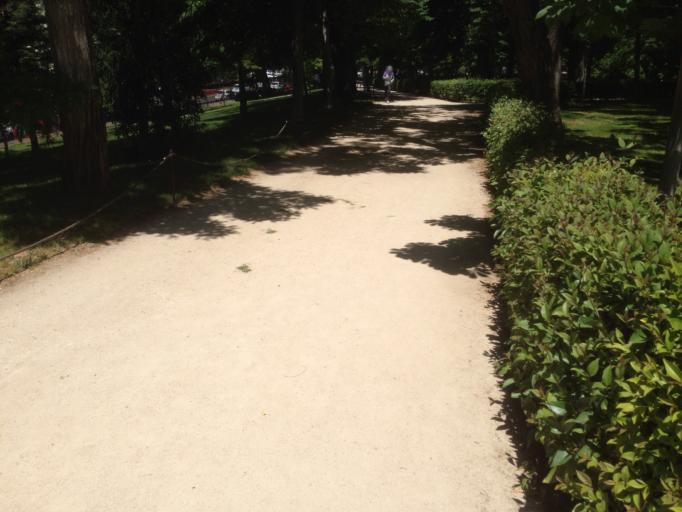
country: ES
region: Madrid
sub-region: Provincia de Madrid
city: Retiro
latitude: 40.4181
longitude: -3.6883
